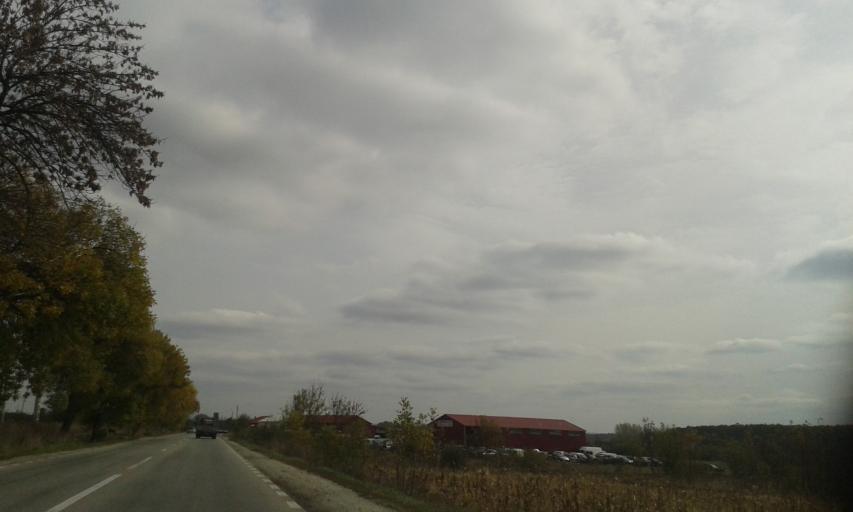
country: RO
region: Gorj
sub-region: Comuna Scoarta
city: Scoarta
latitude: 45.0294
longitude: 23.4232
